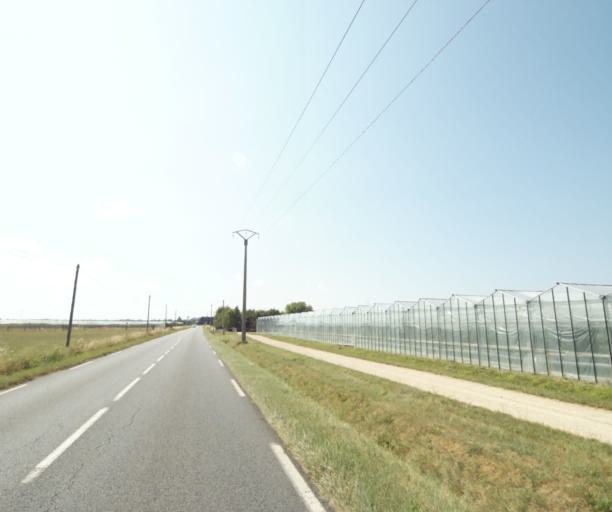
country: FR
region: Centre
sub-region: Departement du Loiret
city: Saint-Cyr-en-Val
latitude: 47.8484
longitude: 1.9560
